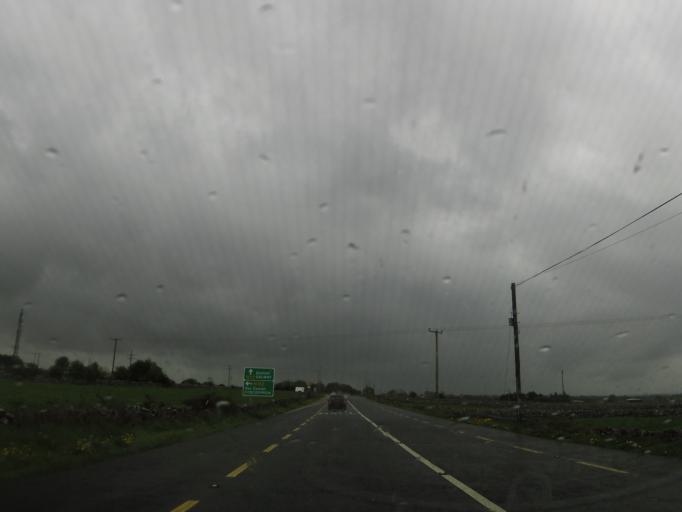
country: IE
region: Connaught
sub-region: County Galway
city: Claregalway
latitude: 53.3642
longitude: -8.9256
